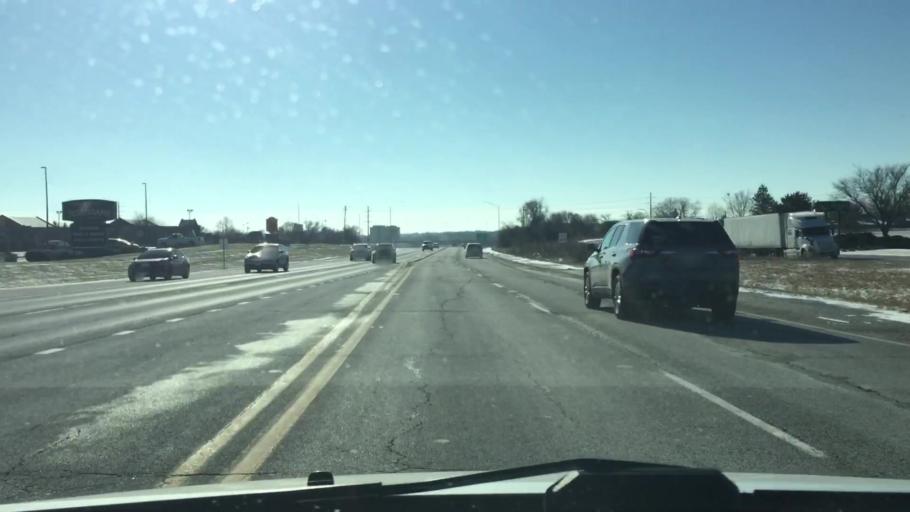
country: US
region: Illinois
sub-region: Kane County
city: Sleepy Hollow
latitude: 42.0732
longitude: -88.2904
